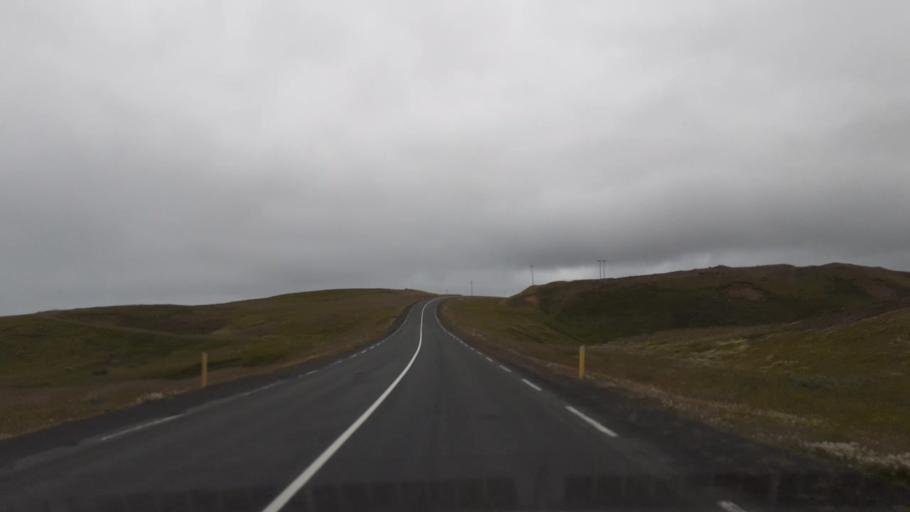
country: IS
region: Northeast
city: Husavik
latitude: 66.1123
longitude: -17.2558
